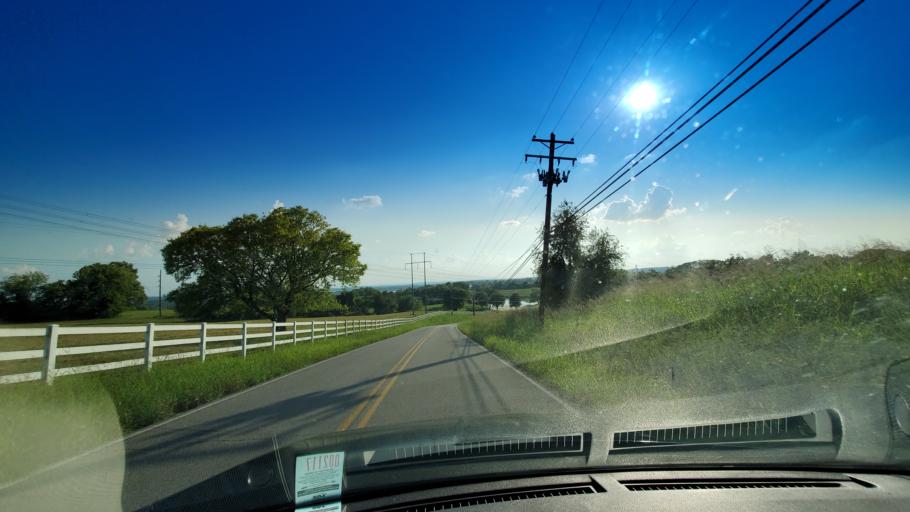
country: US
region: Tennessee
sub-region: Wilson County
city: Rural Hill
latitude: 36.1494
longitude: -86.3872
